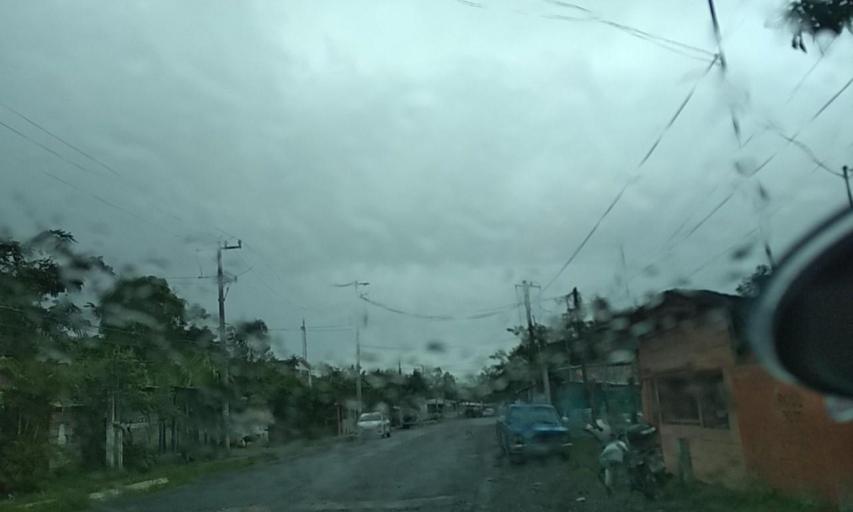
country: MX
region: Veracruz
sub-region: Papantla
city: Residencial Tajin
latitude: 20.6403
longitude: -97.3664
